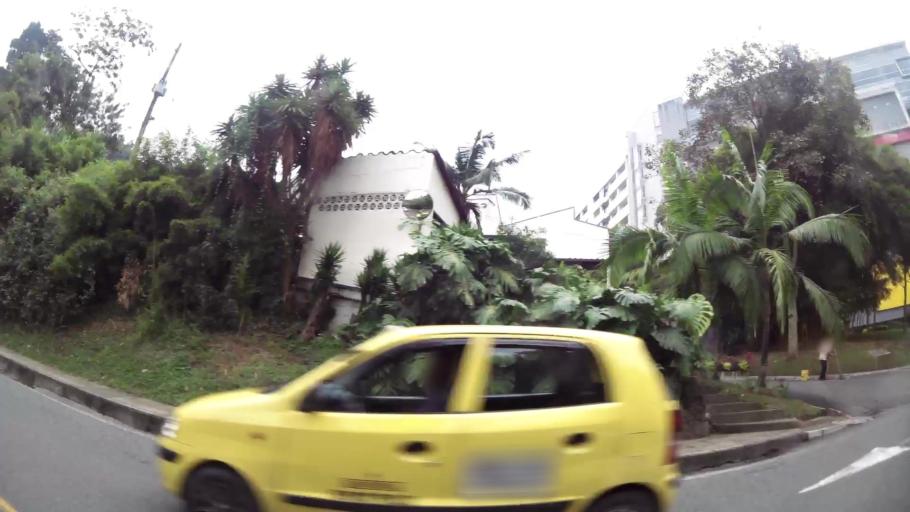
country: CO
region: Antioquia
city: Envigado
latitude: 6.1990
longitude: -75.5577
